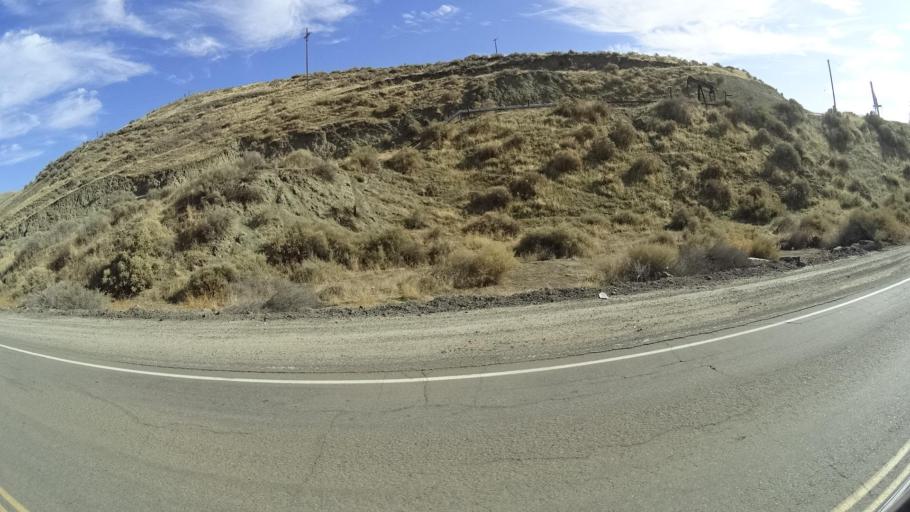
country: US
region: California
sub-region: Kern County
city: Oildale
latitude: 35.5899
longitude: -118.9597
